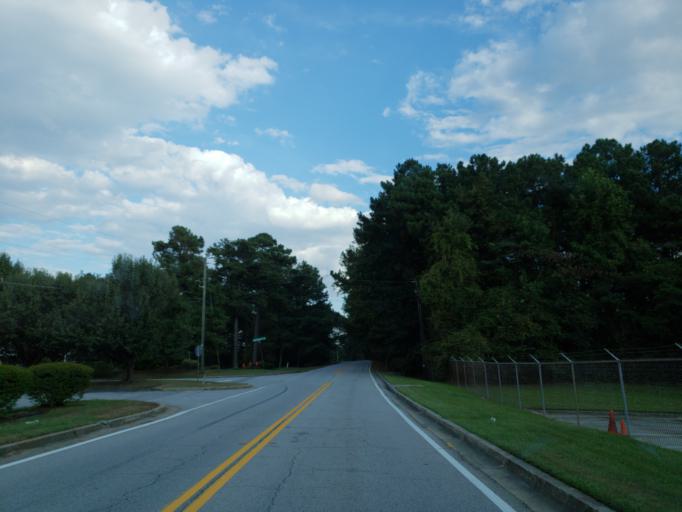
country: US
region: Georgia
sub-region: Cobb County
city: Mableton
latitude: 33.7805
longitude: -84.5399
